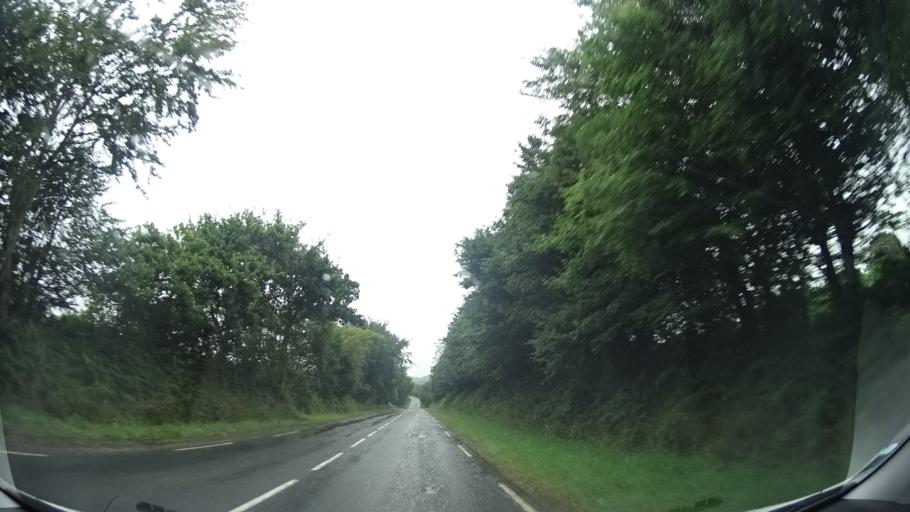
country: FR
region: Lower Normandy
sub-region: Departement de la Manche
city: Martinvast
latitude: 49.6064
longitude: -1.7254
